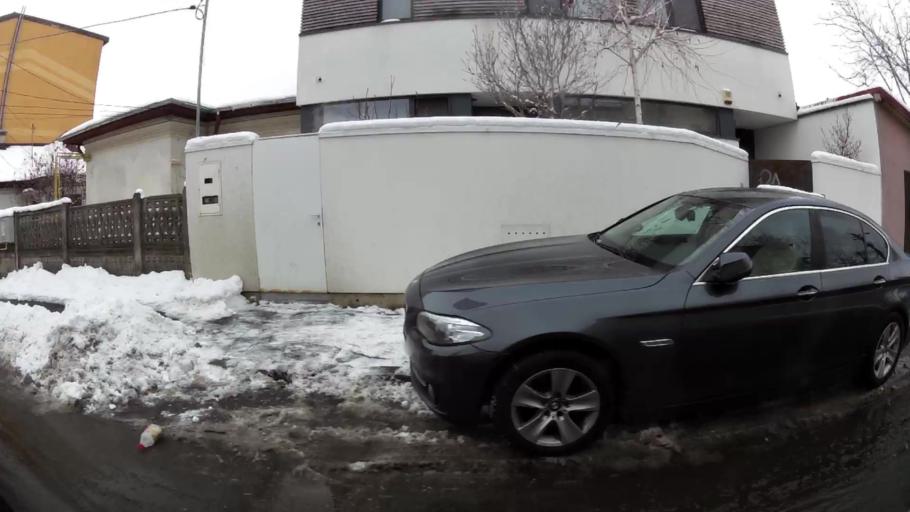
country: RO
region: Bucuresti
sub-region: Municipiul Bucuresti
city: Bucuresti
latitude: 44.3939
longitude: 26.1057
